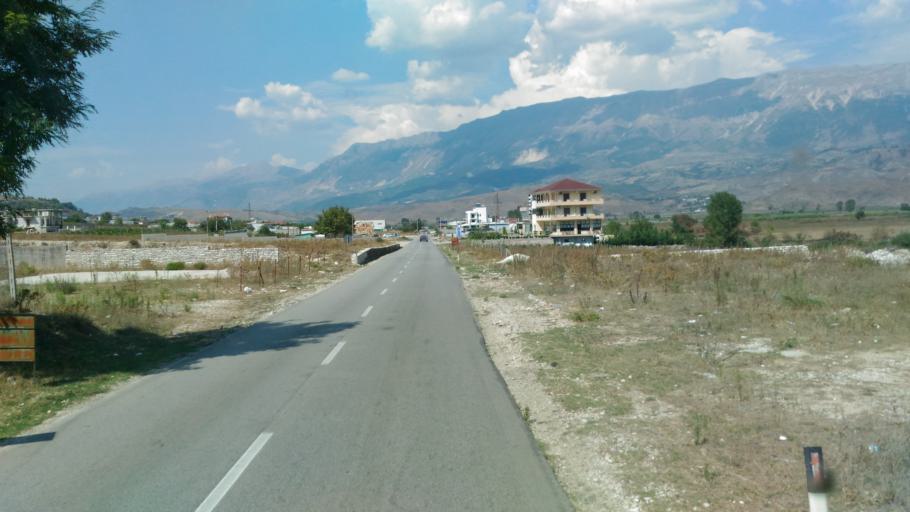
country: AL
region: Gjirokaster
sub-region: Rrethi i Gjirokastres
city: Dervician
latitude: 40.0465
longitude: 20.1766
